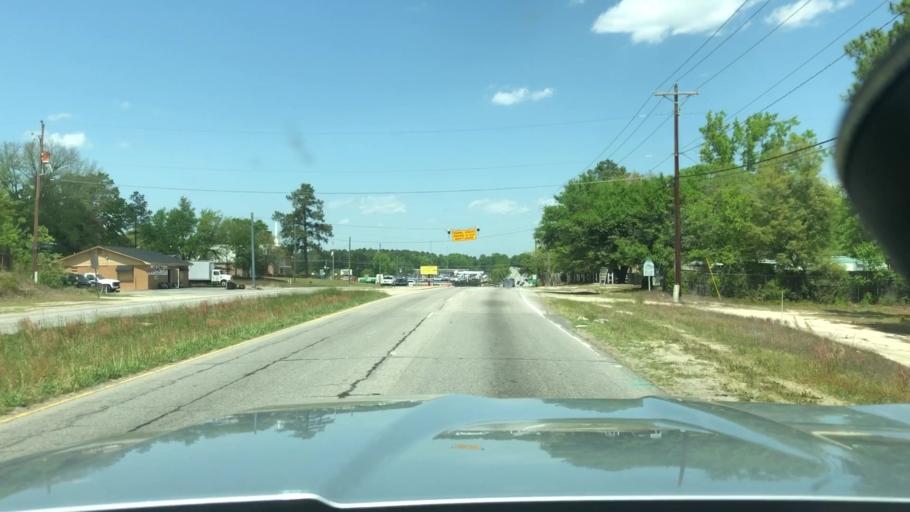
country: US
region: South Carolina
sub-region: Lexington County
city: Pineridge
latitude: 33.8998
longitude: -81.0639
